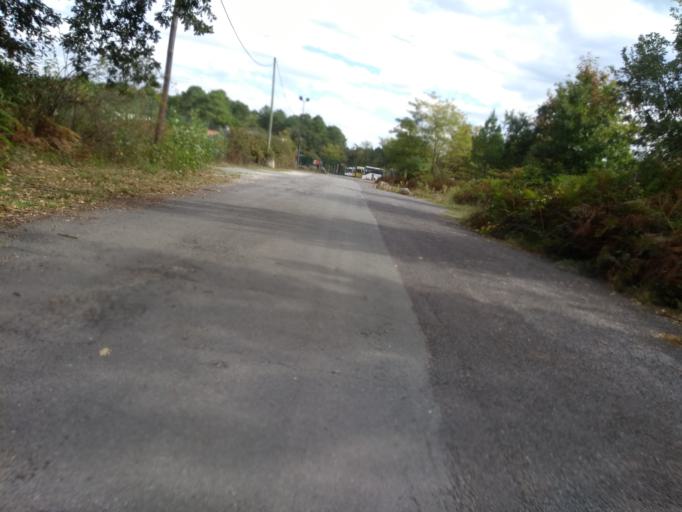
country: FR
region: Aquitaine
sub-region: Departement de la Gironde
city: Cestas
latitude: 44.7464
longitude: -0.6944
